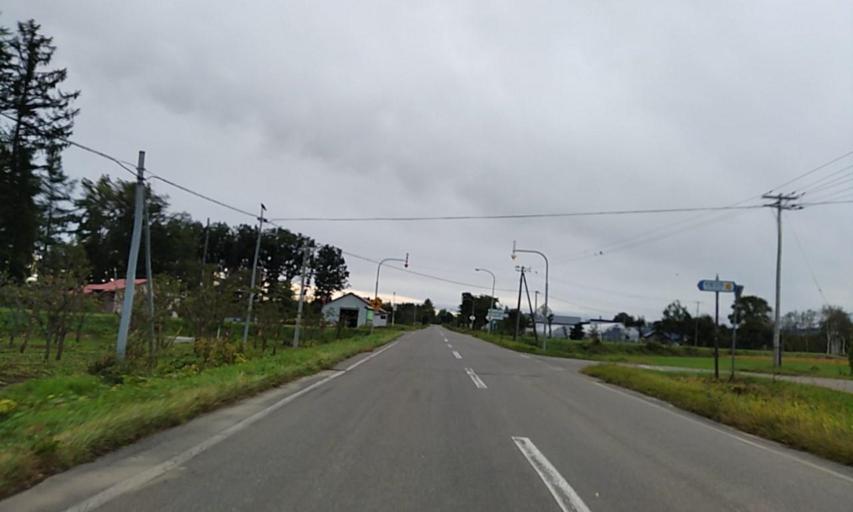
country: JP
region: Hokkaido
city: Obihiro
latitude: 42.6529
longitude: 143.0856
